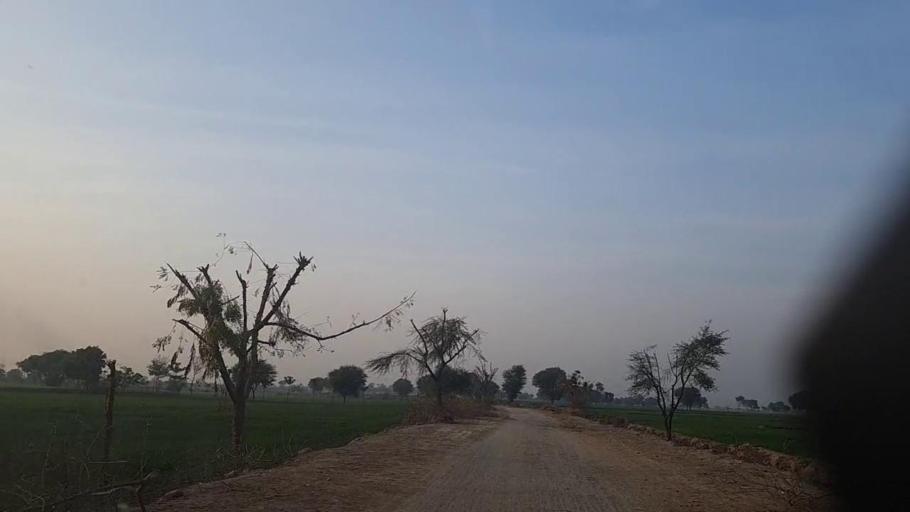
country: PK
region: Sindh
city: Sakrand
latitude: 26.1328
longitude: 68.2286
